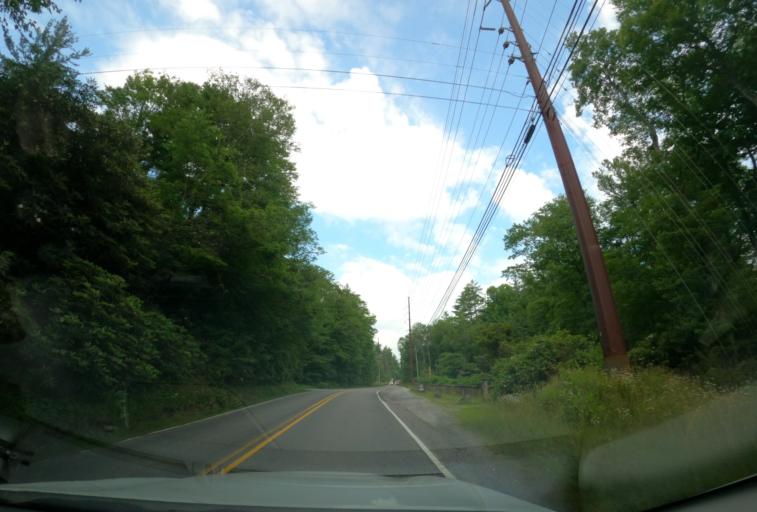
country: US
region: North Carolina
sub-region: Macon County
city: Franklin
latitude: 35.0860
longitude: -83.1771
